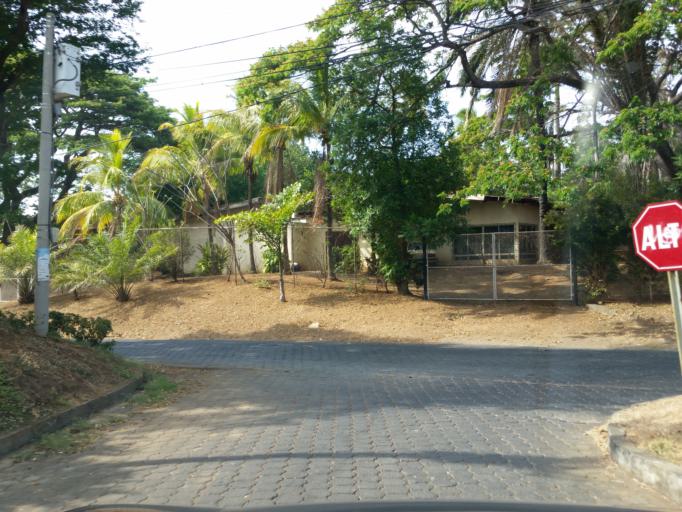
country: NI
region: Managua
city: Managua
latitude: 12.0942
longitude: -86.2297
